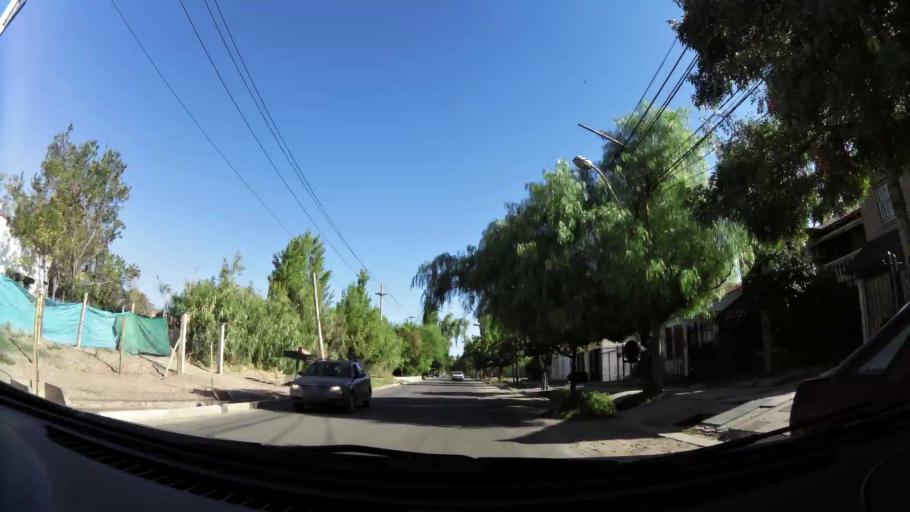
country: AR
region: Mendoza
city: Mendoza
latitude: -32.9054
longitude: -68.8182
